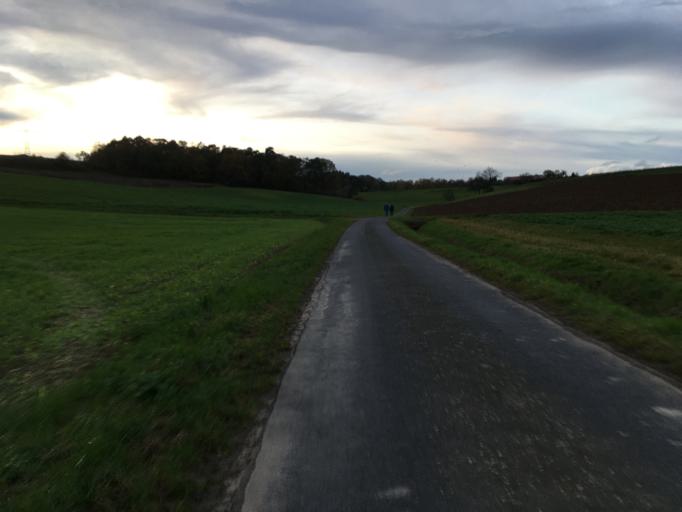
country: DE
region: Baden-Wuerttemberg
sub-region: Karlsruhe Region
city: Rosenberg
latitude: 49.3932
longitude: 9.4889
